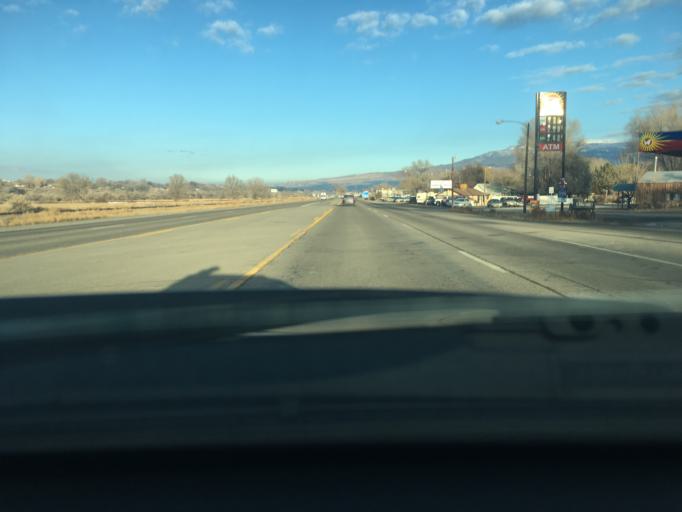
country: US
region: Colorado
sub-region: Delta County
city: Delta
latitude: 38.7268
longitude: -108.0659
